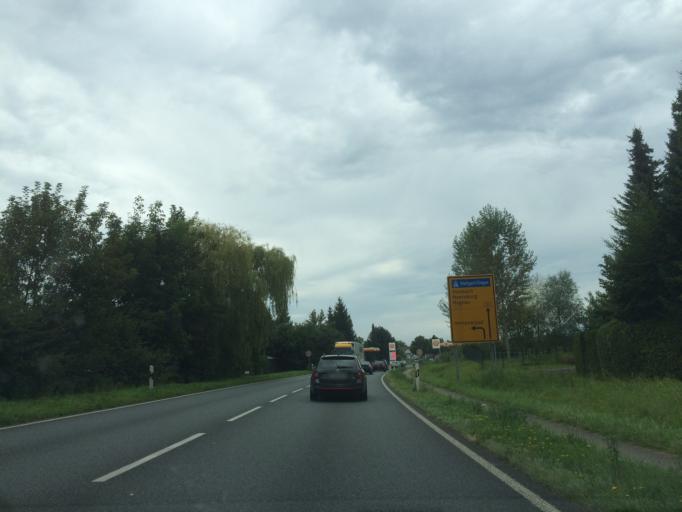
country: DE
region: Baden-Wuerttemberg
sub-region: Tuebingen Region
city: Immenstaad am Bodensee
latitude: 47.6666
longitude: 9.3607
